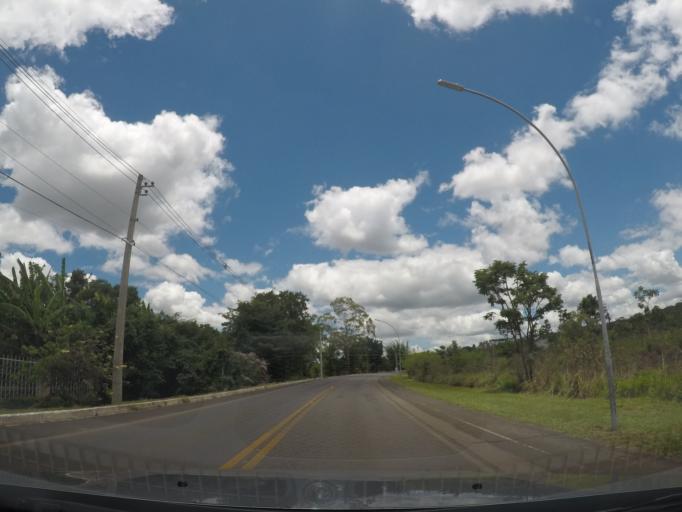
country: BR
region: Federal District
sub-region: Brasilia
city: Brasilia
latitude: -15.7707
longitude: -47.8131
